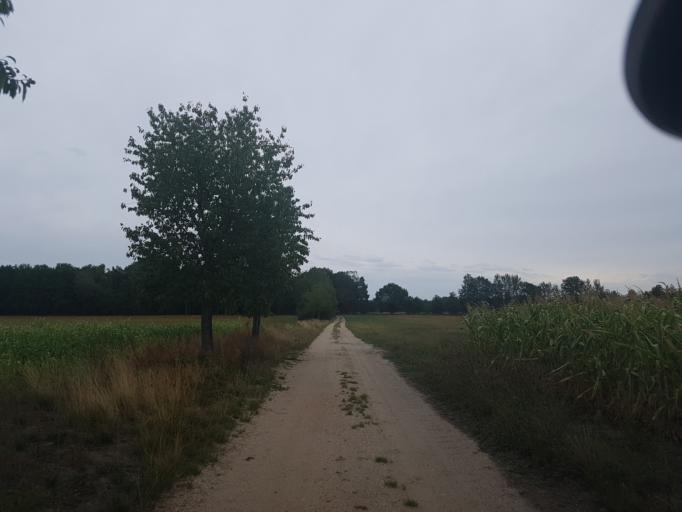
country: DE
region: Brandenburg
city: Finsterwalde
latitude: 51.6059
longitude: 13.6492
